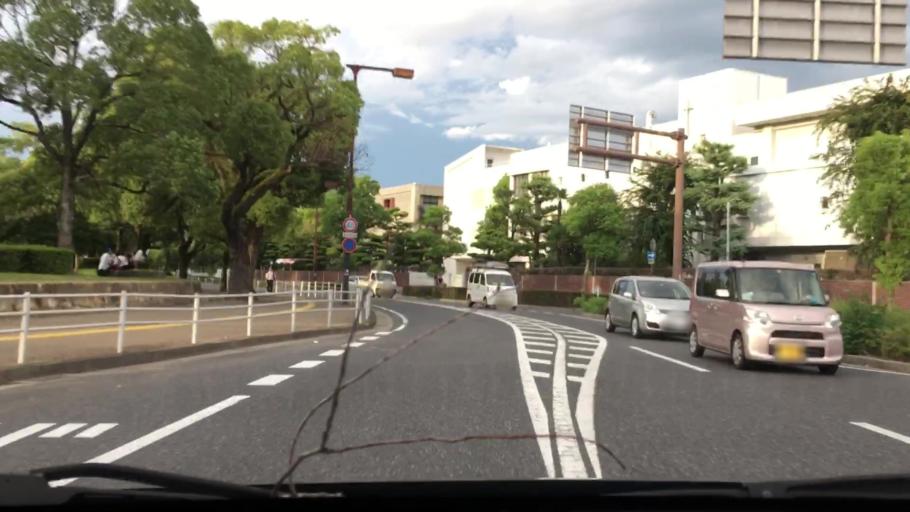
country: JP
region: Hyogo
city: Himeji
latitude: 34.8355
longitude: 134.6960
